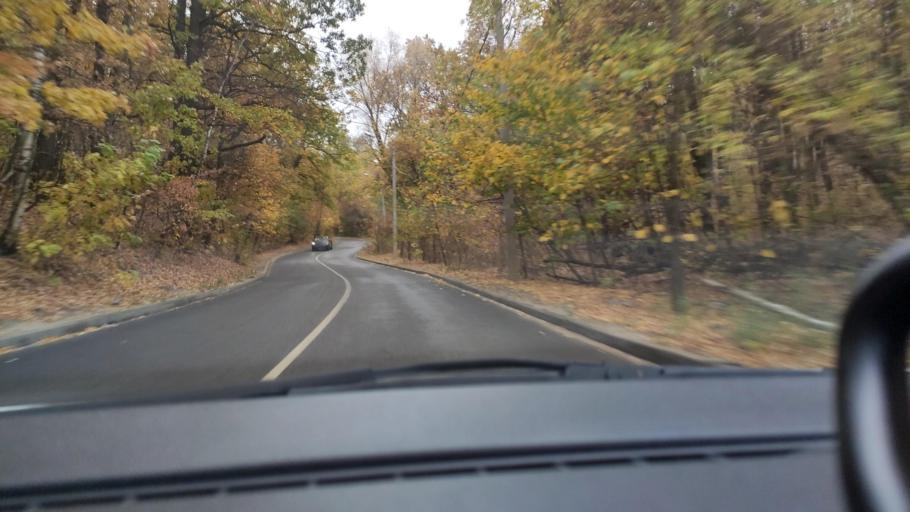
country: RU
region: Voronezj
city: Voronezh
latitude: 51.7201
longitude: 39.2350
